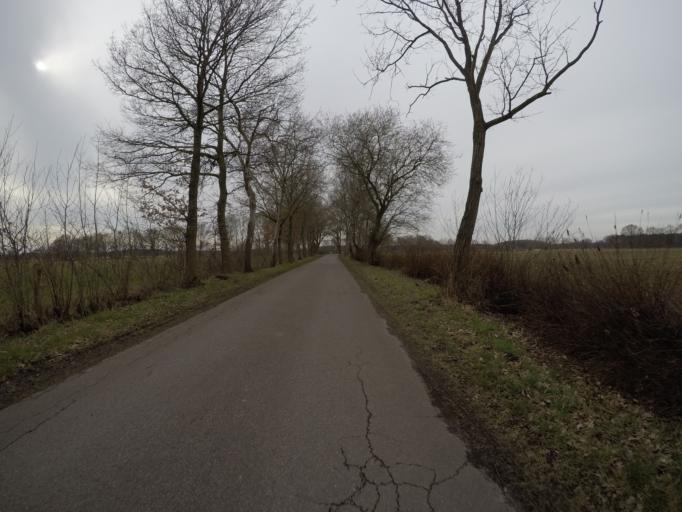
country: DE
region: North Rhine-Westphalia
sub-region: Regierungsbezirk Munster
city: Rhede
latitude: 51.7752
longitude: 6.6719
